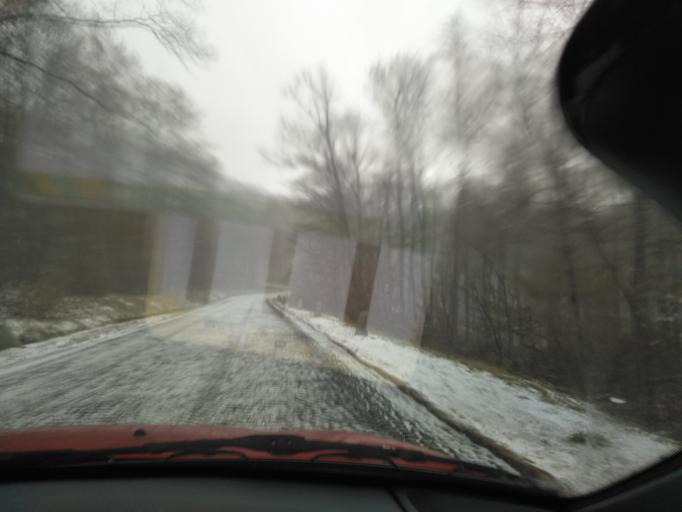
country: AT
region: Lower Austria
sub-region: Politischer Bezirk Wien-Umgebung
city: Klosterneuburg
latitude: 48.2594
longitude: 16.2902
